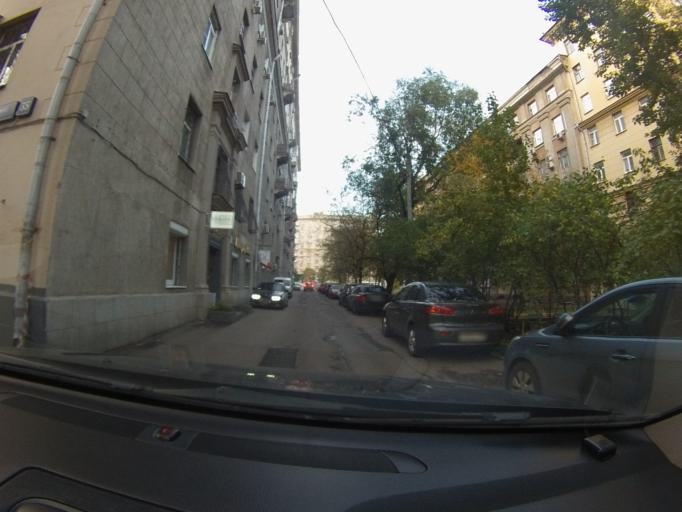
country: RU
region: Moskovskaya
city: Presnenskiy
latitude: 55.7404
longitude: 37.5400
